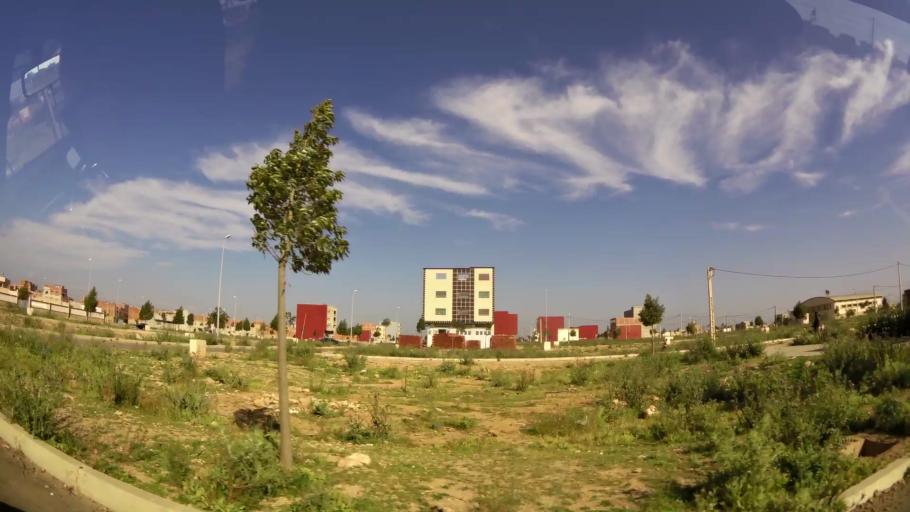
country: MA
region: Oriental
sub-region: Oujda-Angad
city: Oujda
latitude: 34.7188
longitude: -1.8886
